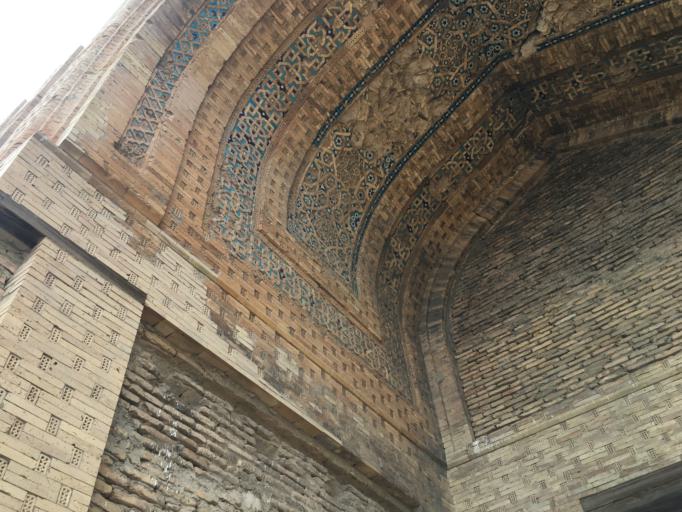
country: TM
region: Dasoguz
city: Koeneuergench
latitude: 42.2977
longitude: 59.1454
